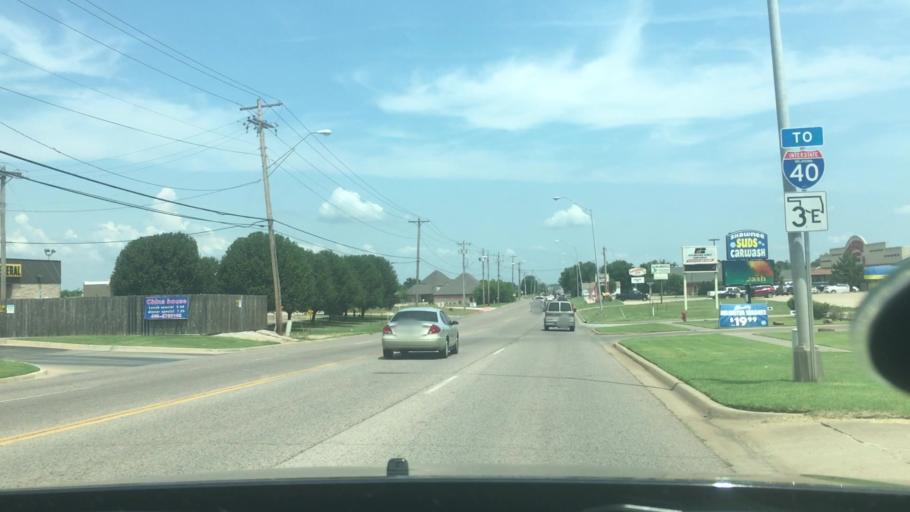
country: US
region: Oklahoma
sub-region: Pottawatomie County
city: Shawnee
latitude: 35.3630
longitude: -96.9298
